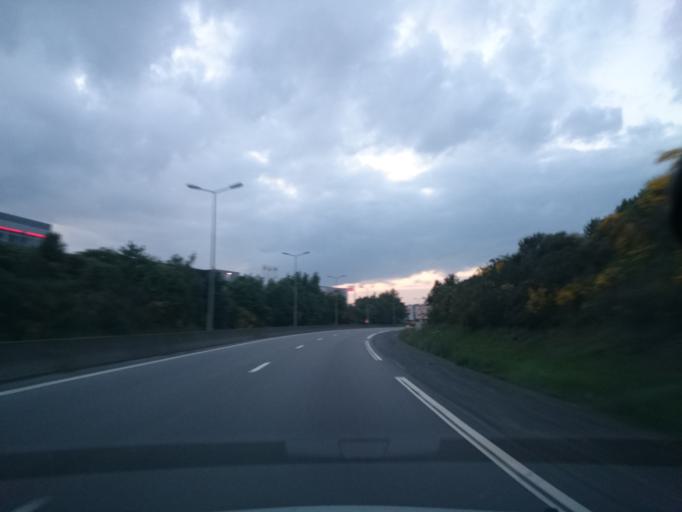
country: FR
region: Brittany
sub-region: Departement d'Ille-et-Vilaine
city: Chantepie
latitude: 48.1051
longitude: -1.6149
